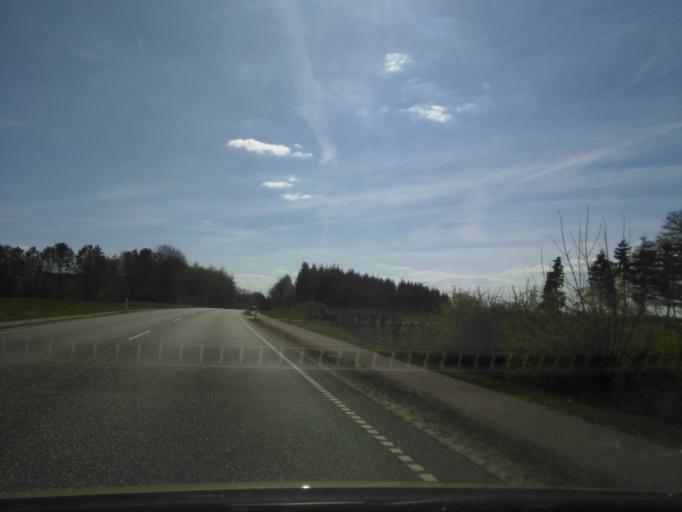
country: DK
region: Central Jutland
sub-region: Silkeborg Kommune
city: Kjellerup
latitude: 56.3382
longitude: 9.3453
